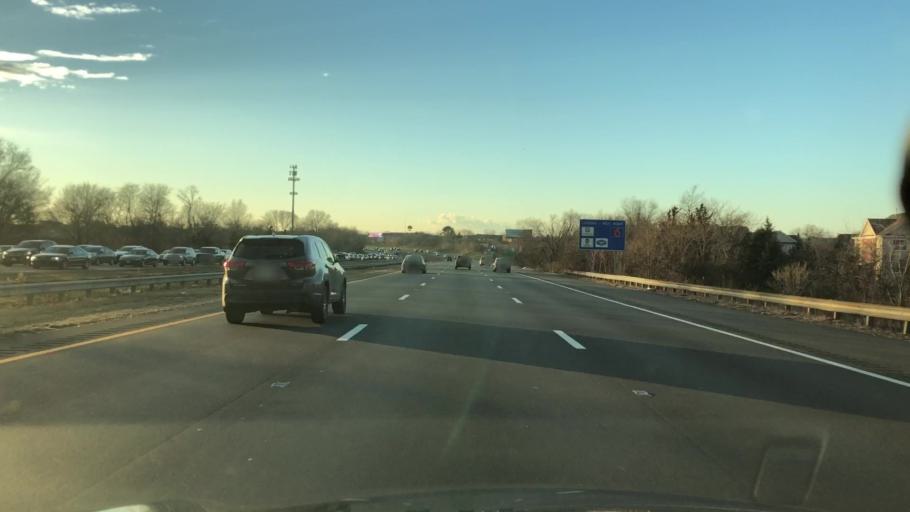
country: US
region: New Jersey
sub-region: Middlesex County
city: South Plainfield
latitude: 40.5548
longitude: -74.4167
